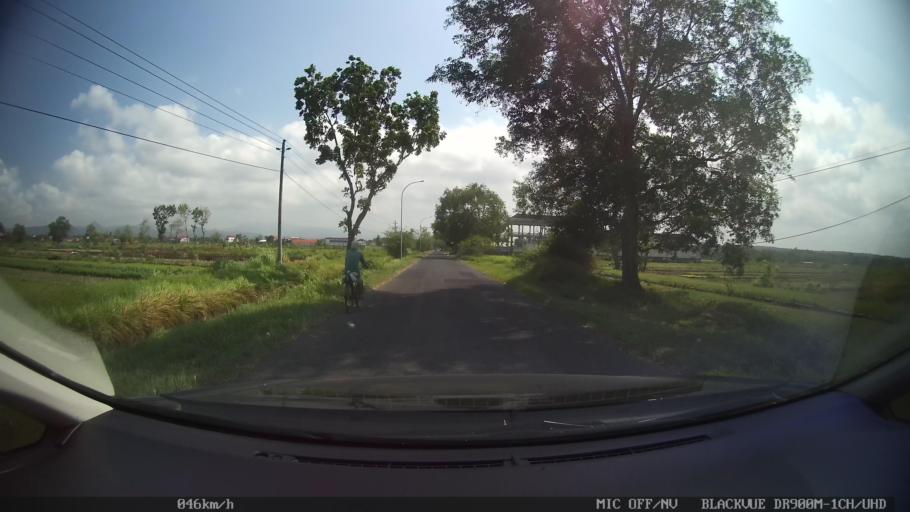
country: ID
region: Daerah Istimewa Yogyakarta
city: Srandakan
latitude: -7.9000
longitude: 110.1525
